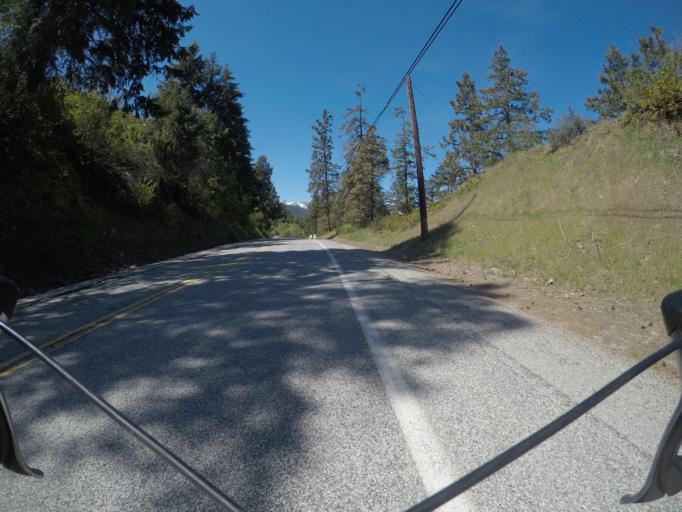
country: US
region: Washington
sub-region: Chelan County
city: Cashmere
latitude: 47.5303
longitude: -120.5205
